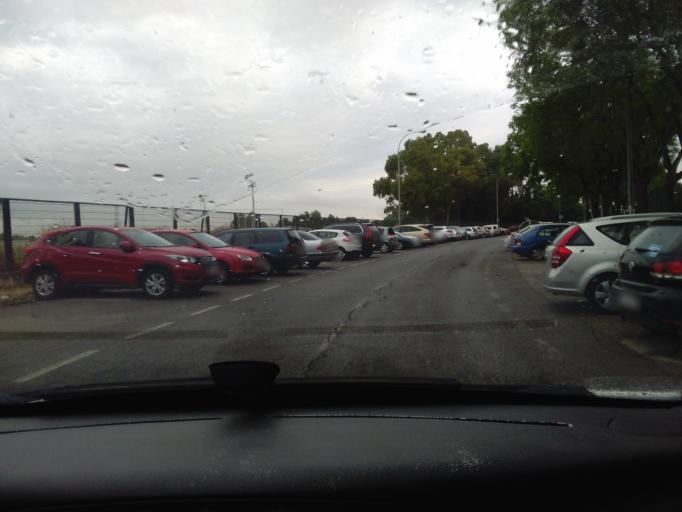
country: ES
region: Andalusia
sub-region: Provincia de Sevilla
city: Sevilla
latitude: 37.4011
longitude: -5.9362
